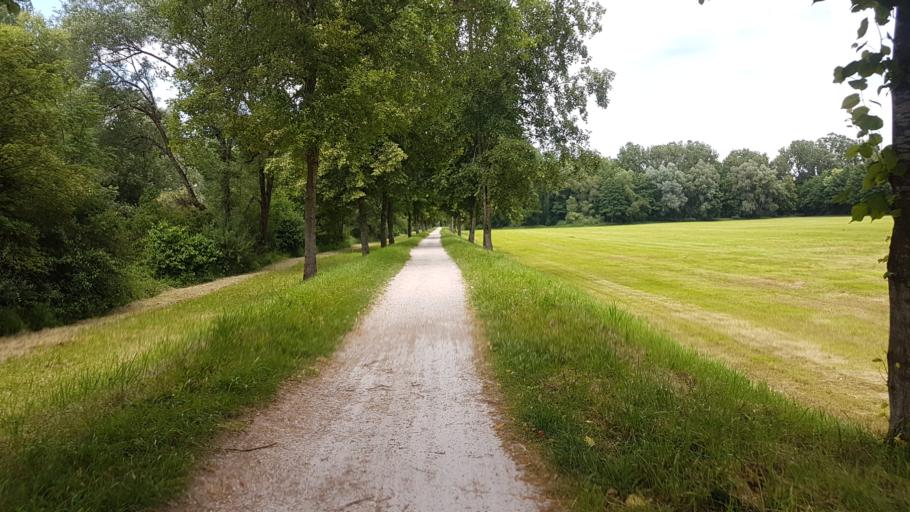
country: DE
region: Baden-Wuerttemberg
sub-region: Tuebingen Region
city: Neufra
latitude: 48.1347
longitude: 9.4642
